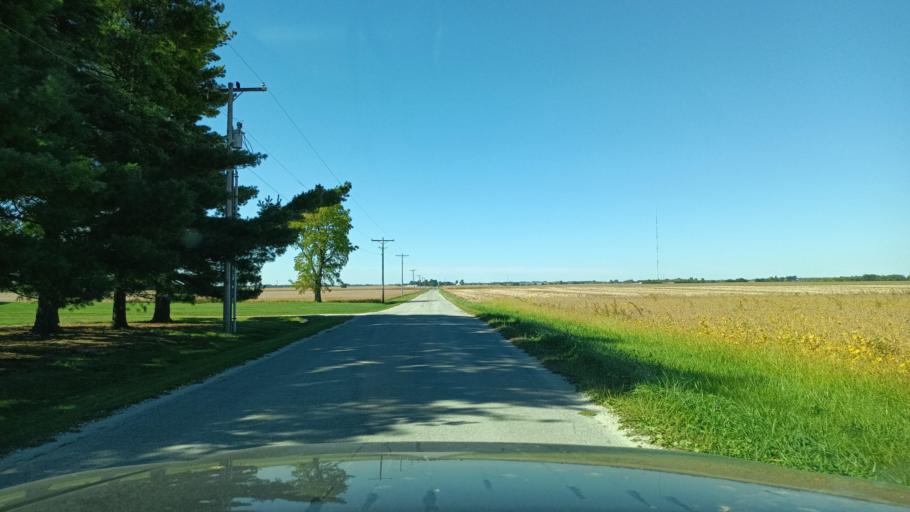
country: US
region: Illinois
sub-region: Champaign County
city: Mahomet
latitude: 40.0987
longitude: -88.4203
